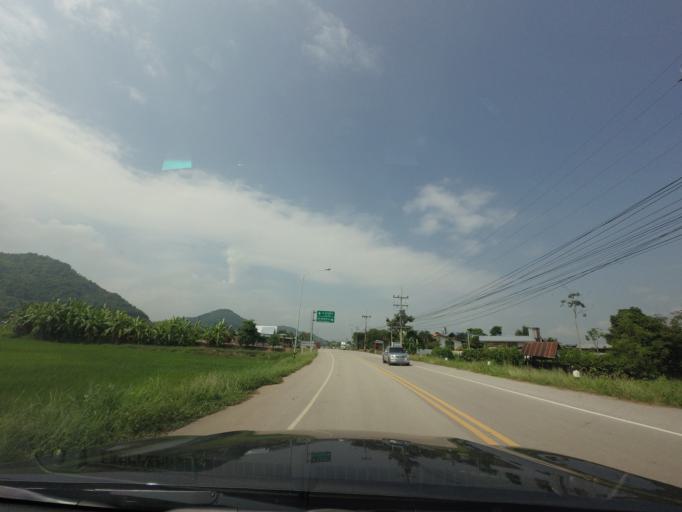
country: LA
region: Xiagnabouli
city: Muang Kenthao
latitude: 17.6864
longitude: 101.3943
